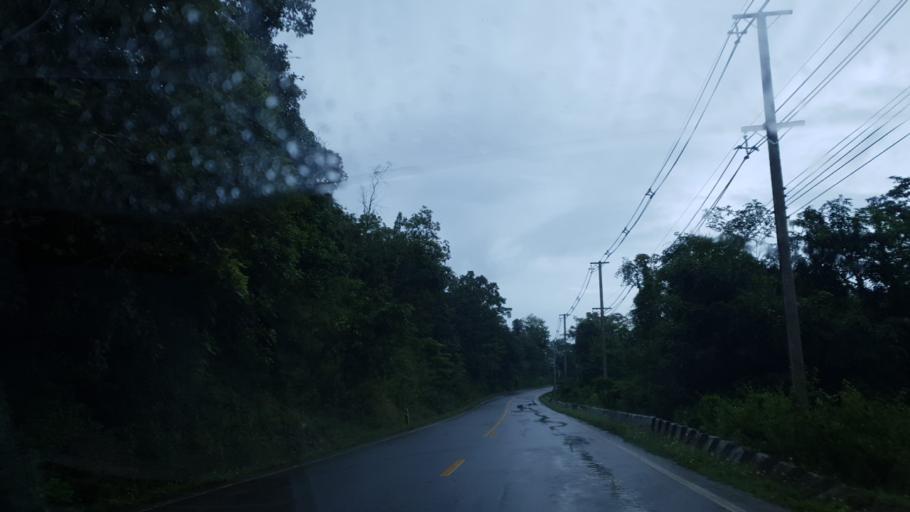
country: TH
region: Mae Hong Son
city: Ban Huai I Huak
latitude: 18.1367
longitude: 98.1758
